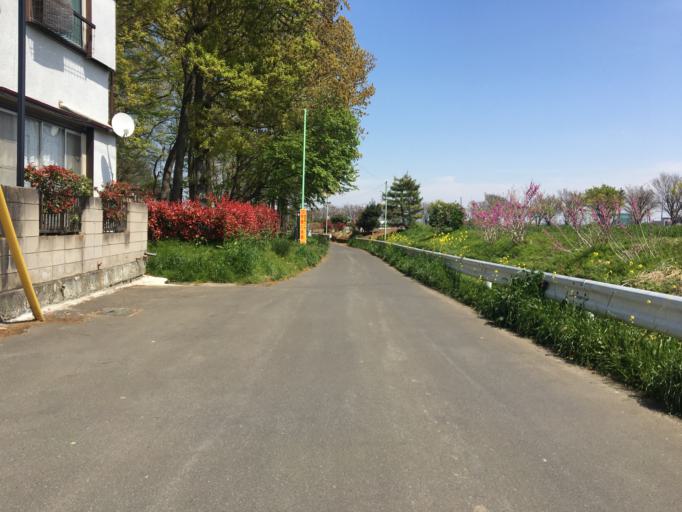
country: JP
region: Saitama
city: Shiki
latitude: 35.8371
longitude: 139.5623
